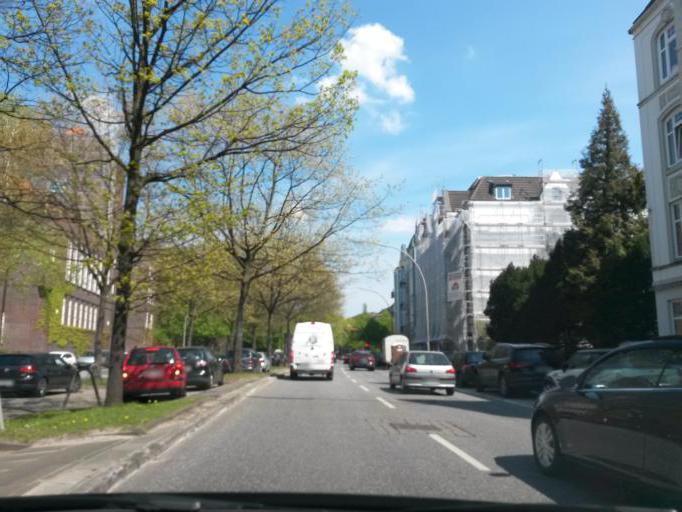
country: DE
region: Hamburg
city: Hamburg-Nord
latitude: 53.5869
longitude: 9.9752
